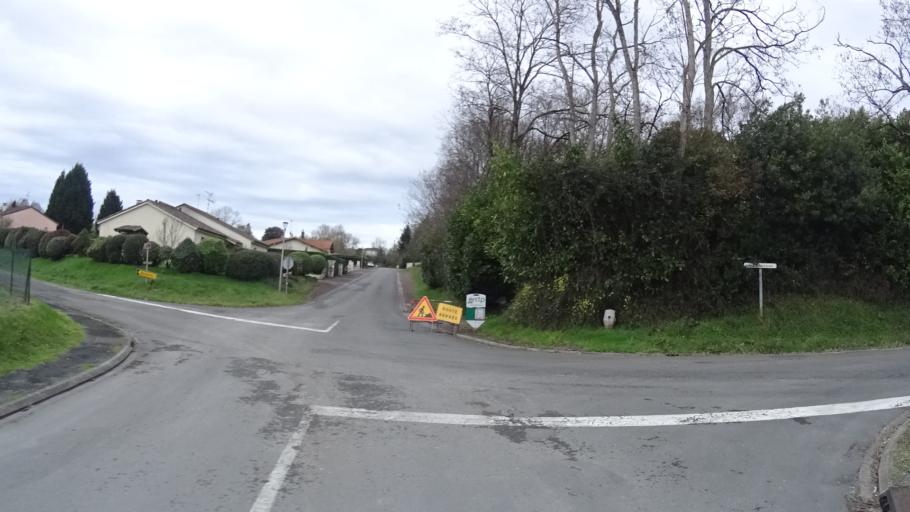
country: FR
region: Aquitaine
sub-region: Departement de la Dordogne
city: Saint-Aulaye
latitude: 45.2020
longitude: 0.1309
